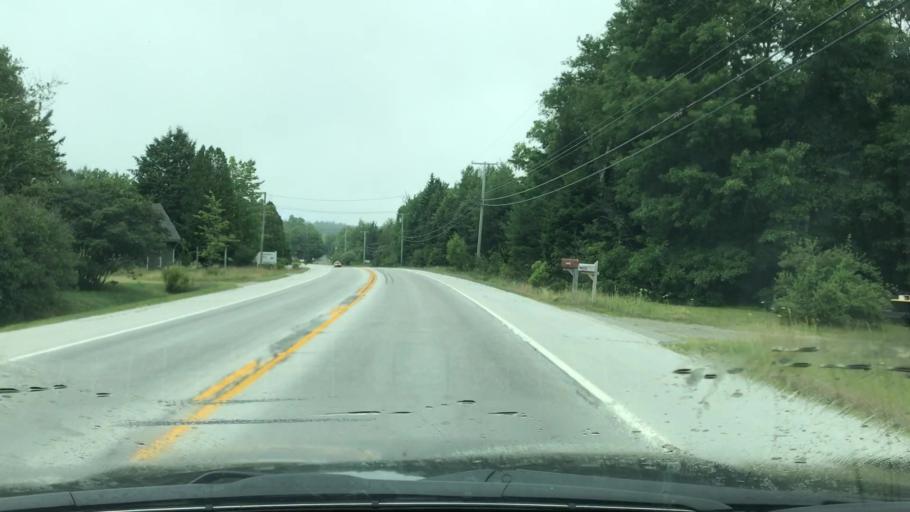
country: US
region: Maine
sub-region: Waldo County
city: Northport
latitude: 44.3300
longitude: -68.9578
